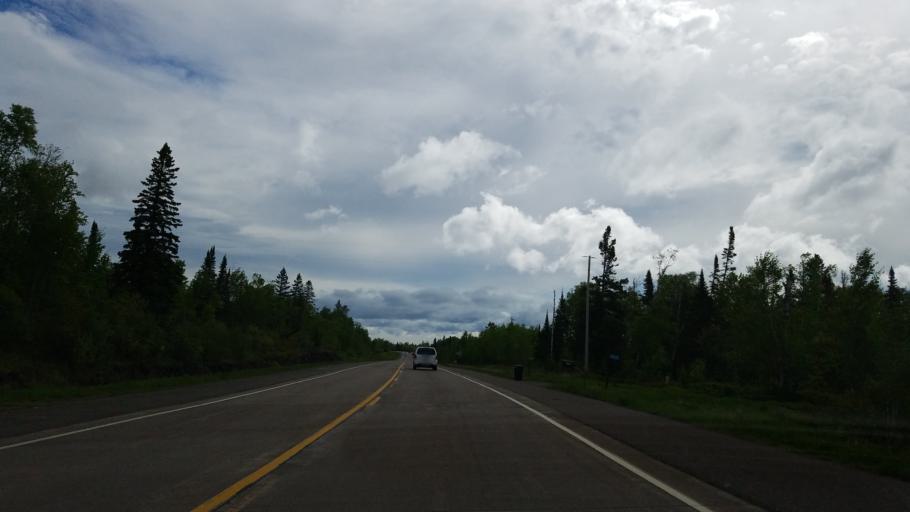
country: US
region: Minnesota
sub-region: Lake County
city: Two Harbors
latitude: 47.1042
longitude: -91.5322
